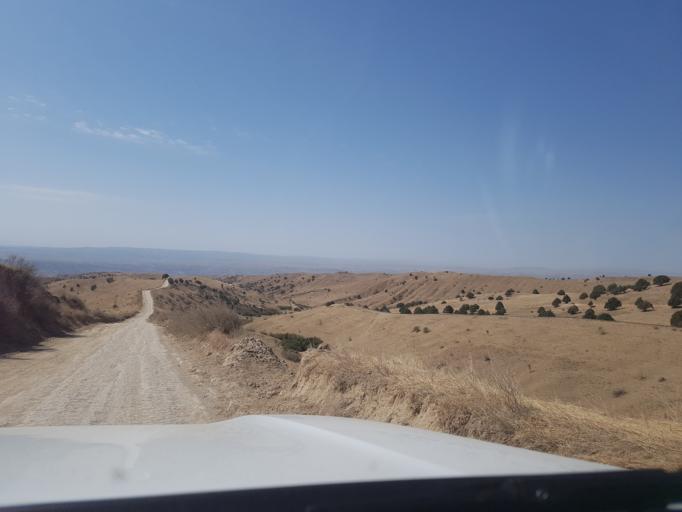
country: TM
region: Ahal
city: Baharly
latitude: 38.3035
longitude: 56.9449
